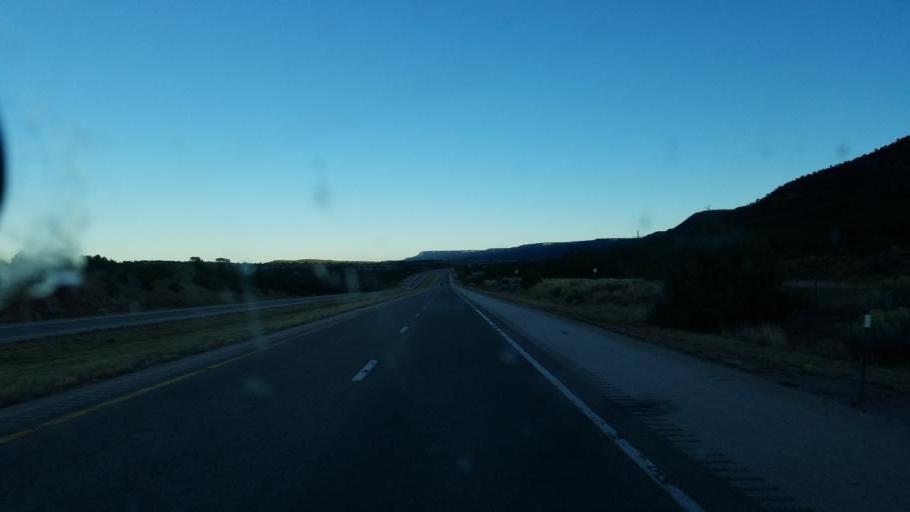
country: US
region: New Mexico
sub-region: San Miguel County
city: Pecos
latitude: 35.4730
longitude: -105.6555
